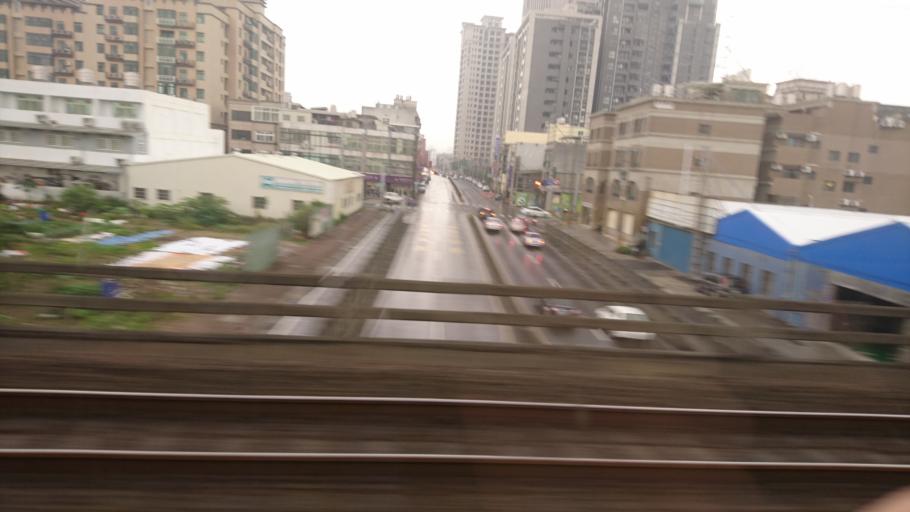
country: TW
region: Taiwan
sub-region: Hsinchu
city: Zhubei
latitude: 24.8280
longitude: 121.0012
